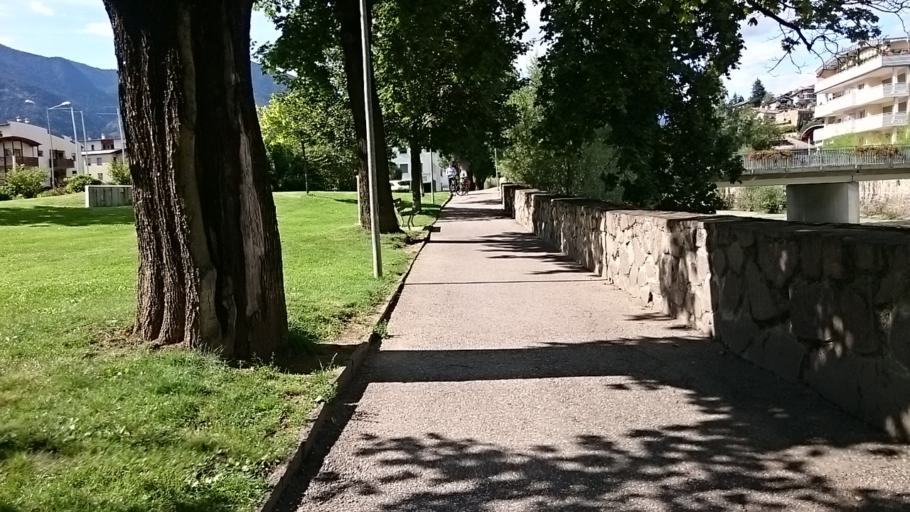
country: IT
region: Trentino-Alto Adige
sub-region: Bolzano
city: Bressanone
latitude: 46.7227
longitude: 11.6561
